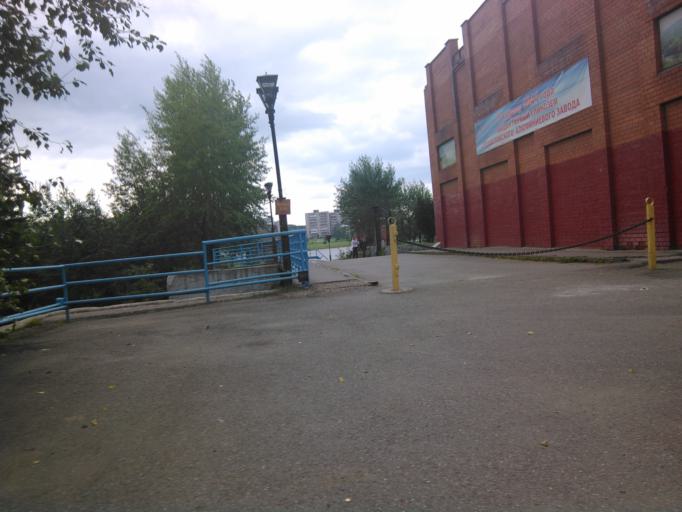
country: RU
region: Sverdlovsk
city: Krasnotur'insk
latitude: 59.7607
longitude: 60.1776
